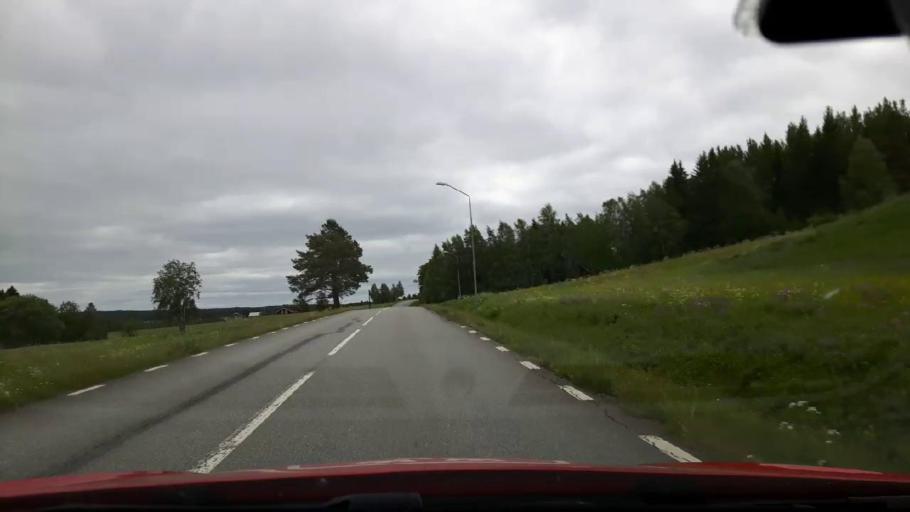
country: SE
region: Jaemtland
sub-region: Stroemsunds Kommun
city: Stroemsund
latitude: 63.5684
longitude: 15.3899
